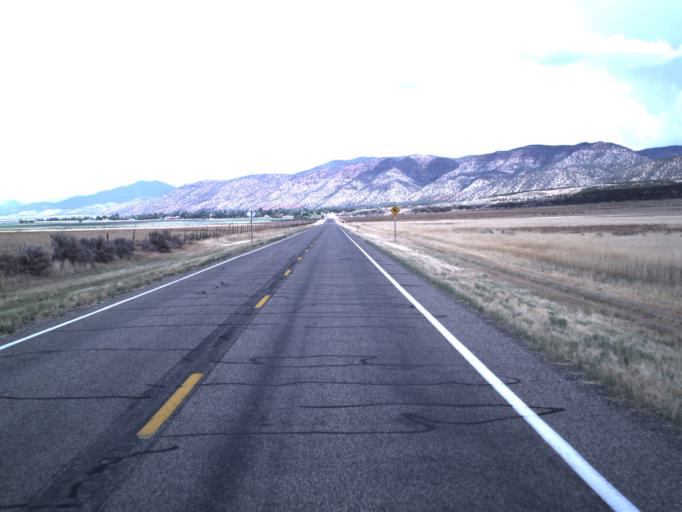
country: US
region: Utah
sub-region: Iron County
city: Parowan
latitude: 37.8650
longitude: -112.8040
